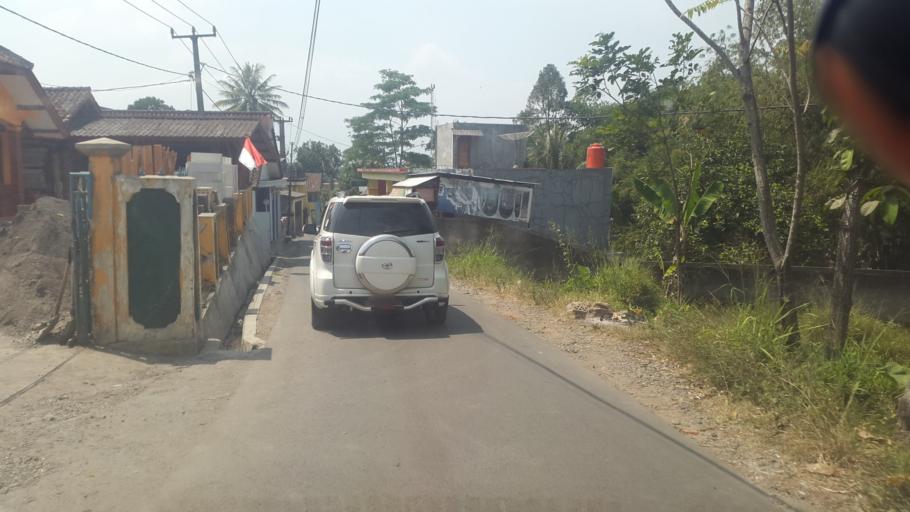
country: ID
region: West Java
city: Cicurug
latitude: -6.7805
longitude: 106.7449
